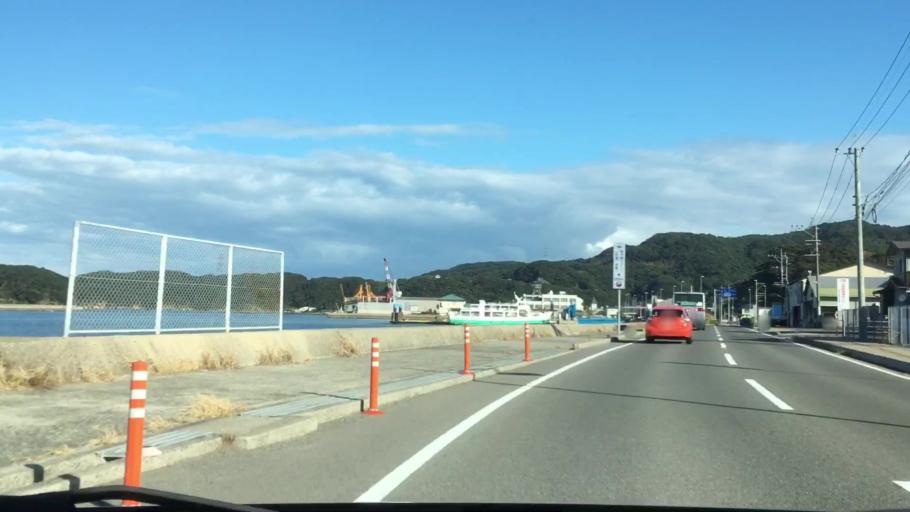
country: JP
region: Nagasaki
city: Togitsu
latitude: 32.9376
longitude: 129.6388
